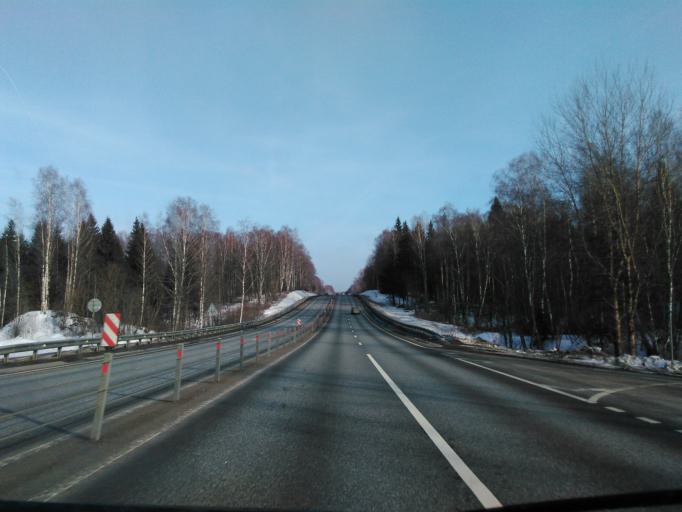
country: RU
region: Smolensk
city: Vyaz'ma
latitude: 55.1891
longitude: 34.0230
